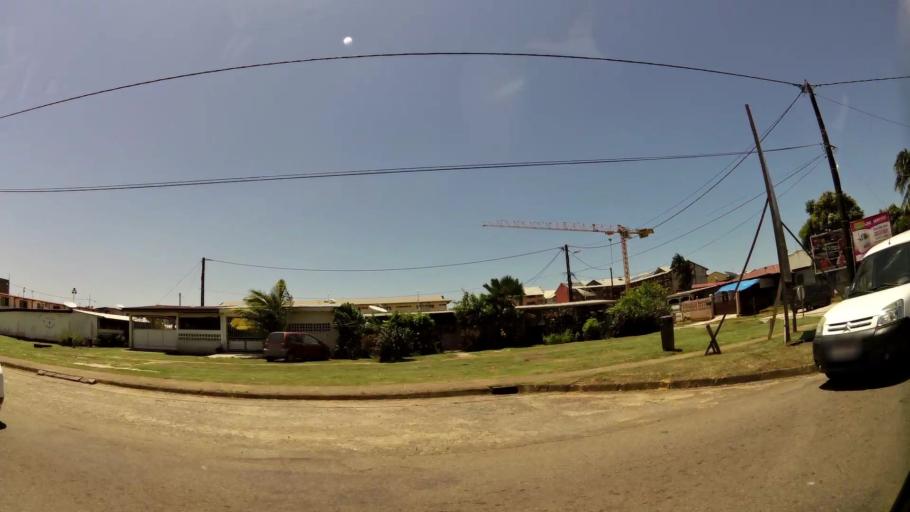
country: GF
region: Guyane
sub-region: Guyane
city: Cayenne
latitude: 4.9322
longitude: -52.3277
